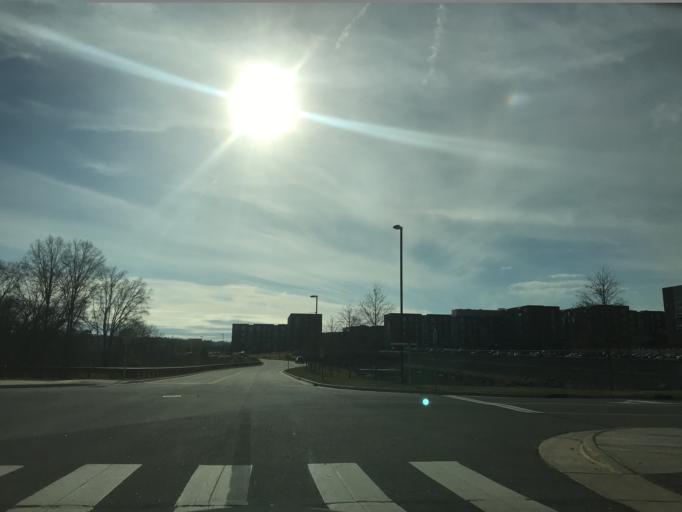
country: US
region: North Carolina
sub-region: Wake County
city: West Raleigh
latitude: 35.7712
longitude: -78.6708
